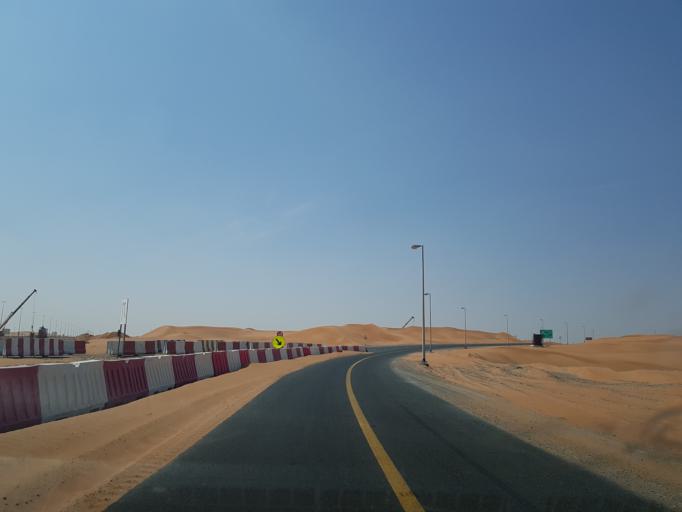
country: AE
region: Ash Shariqah
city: Adh Dhayd
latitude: 25.2488
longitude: 55.8216
